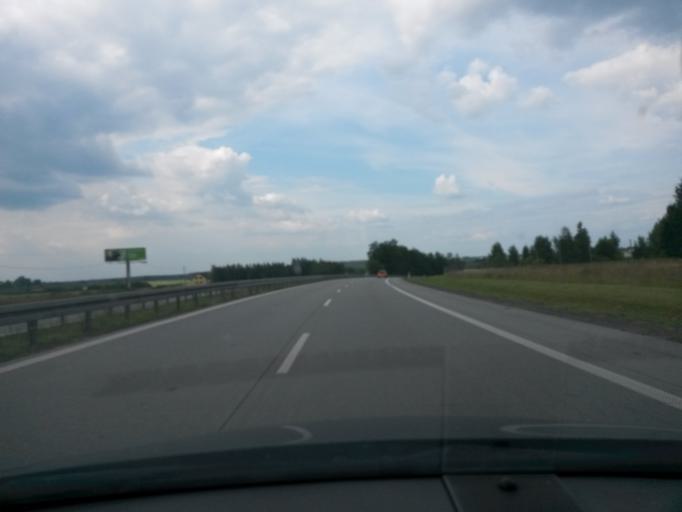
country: PL
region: Lodz Voivodeship
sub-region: Powiat skierniewicki
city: Kowiesy
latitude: 51.8737
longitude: 20.3872
